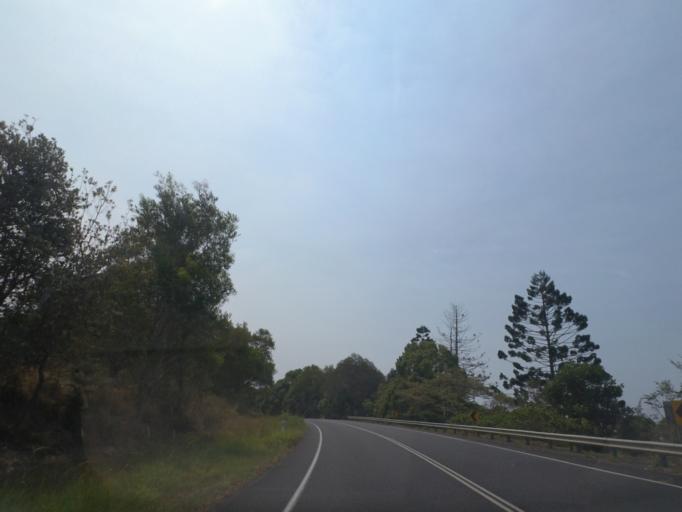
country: AU
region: New South Wales
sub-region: Byron Shire
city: Brunswick Heads
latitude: -28.4925
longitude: 153.5256
